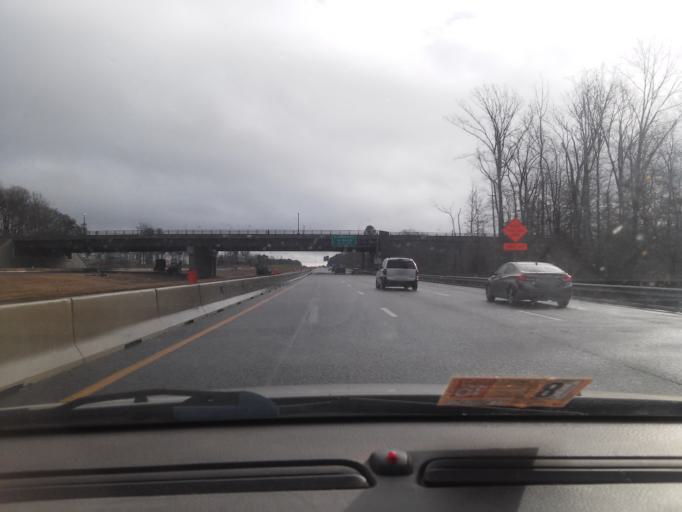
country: US
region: Virginia
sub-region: Henrico County
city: Short Pump
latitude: 37.6631
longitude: -77.6315
